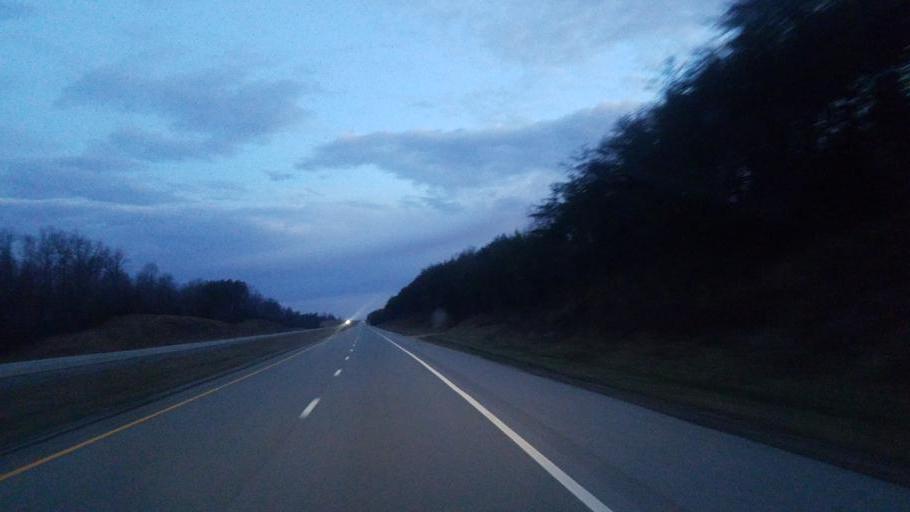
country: US
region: Tennessee
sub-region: Van Buren County
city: Spencer
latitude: 35.6423
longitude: -85.4736
